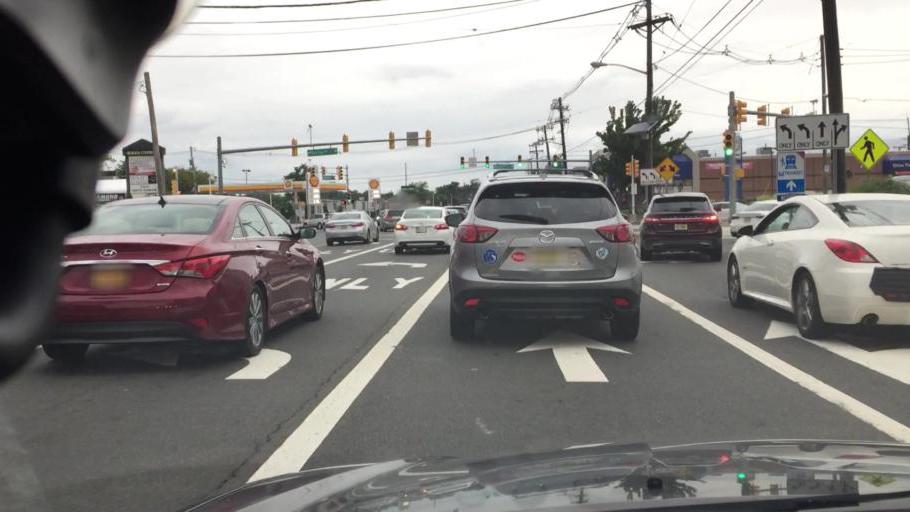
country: US
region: New Jersey
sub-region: Union County
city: Clark
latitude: 40.6298
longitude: -74.3086
